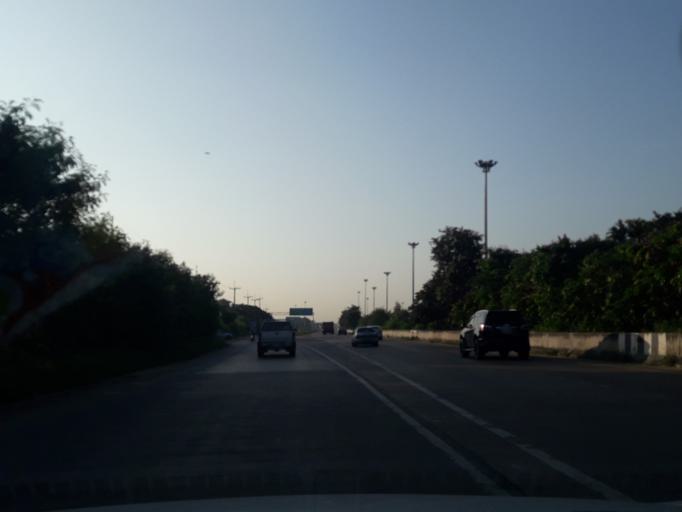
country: TH
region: Phra Nakhon Si Ayutthaya
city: Bang Pa-in
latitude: 14.1633
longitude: 100.5653
